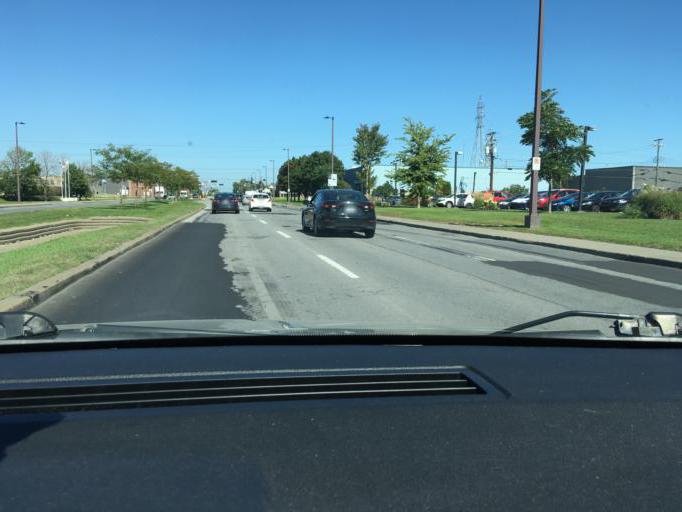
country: CA
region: Quebec
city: Dorval
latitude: 45.5037
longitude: -73.7427
